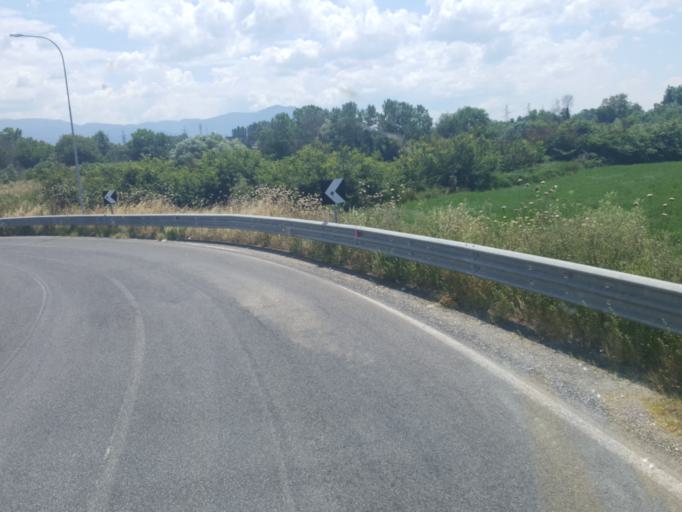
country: IT
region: Latium
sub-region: Citta metropolitana di Roma Capitale
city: Fiano Romano
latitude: 42.1526
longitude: 12.6411
